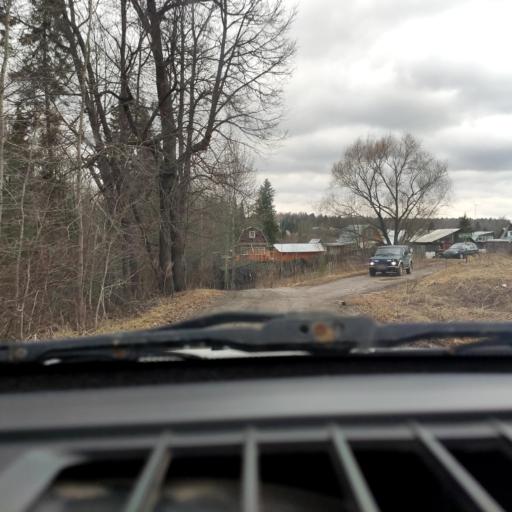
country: RU
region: Perm
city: Kultayevo
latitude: 57.8239
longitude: 55.7889
